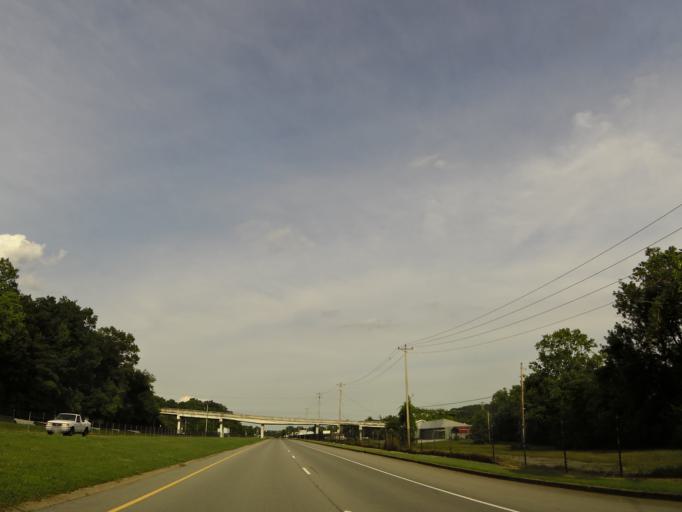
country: US
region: Tennessee
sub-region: Humphreys County
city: Waverly
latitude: 36.0874
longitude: -87.7954
